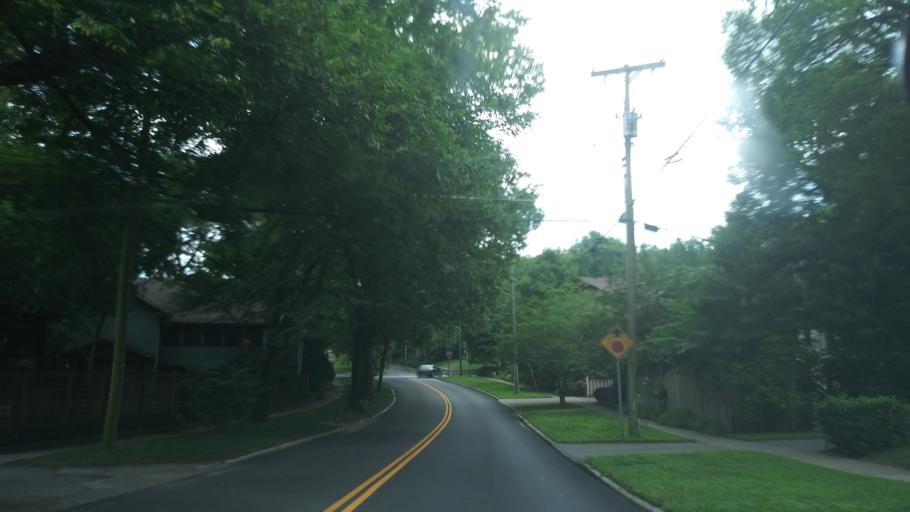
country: US
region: Tennessee
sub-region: Davidson County
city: Nashville
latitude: 36.1378
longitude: -86.8266
